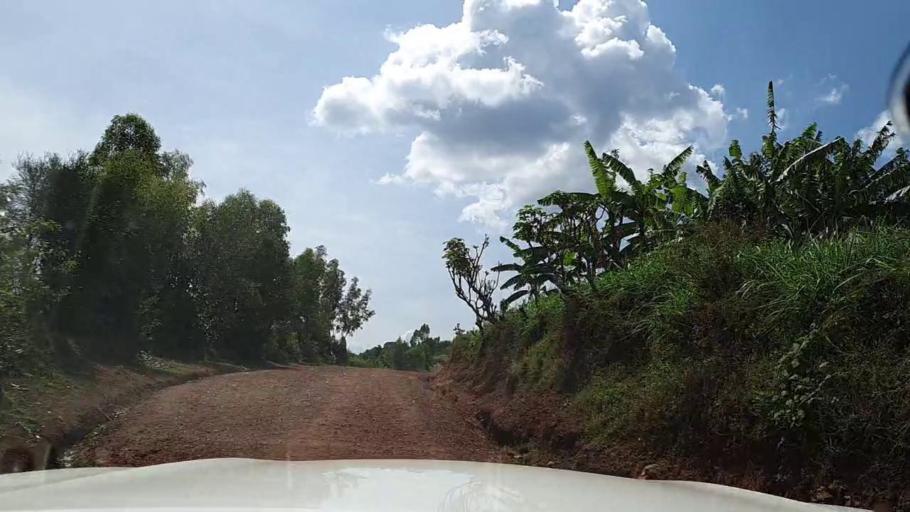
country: RW
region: Southern Province
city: Butare
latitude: -2.7441
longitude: 29.7014
